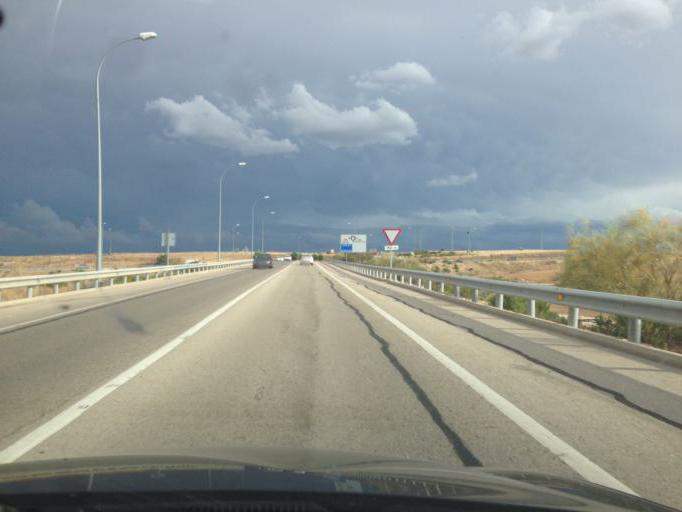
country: ES
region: Madrid
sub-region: Provincia de Madrid
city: Paracuellos de Jarama
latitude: 40.5172
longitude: -3.5051
